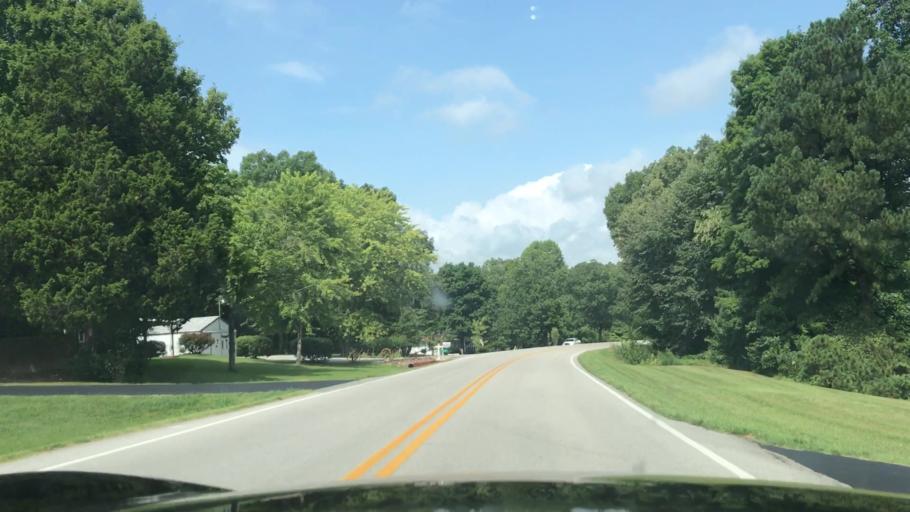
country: US
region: Kentucky
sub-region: Butler County
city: Morgantown
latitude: 37.1824
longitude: -86.8700
